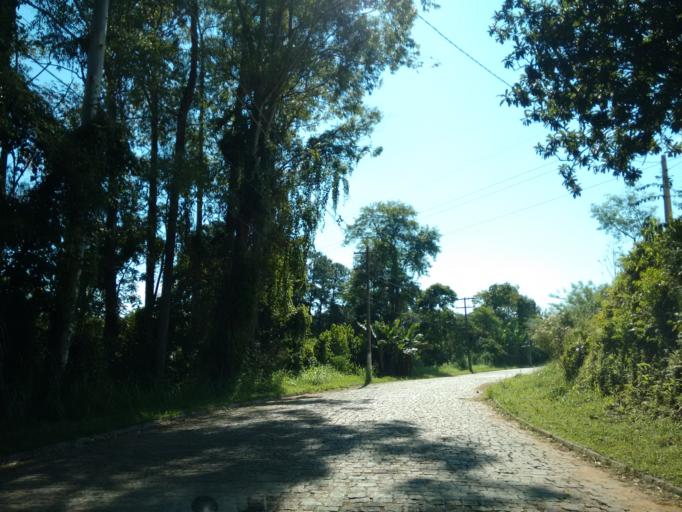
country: BR
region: Santa Catarina
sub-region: Indaial
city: Indaial
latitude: -26.8922
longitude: -49.1916
